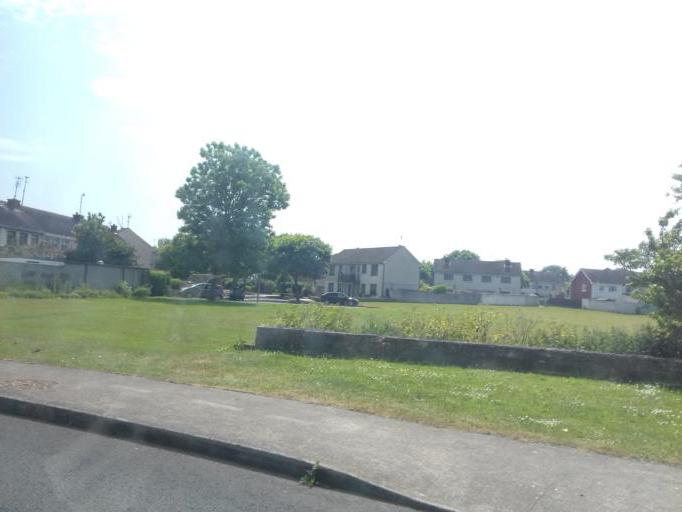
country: IE
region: Leinster
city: Portraine
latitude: 53.4953
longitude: -6.1130
